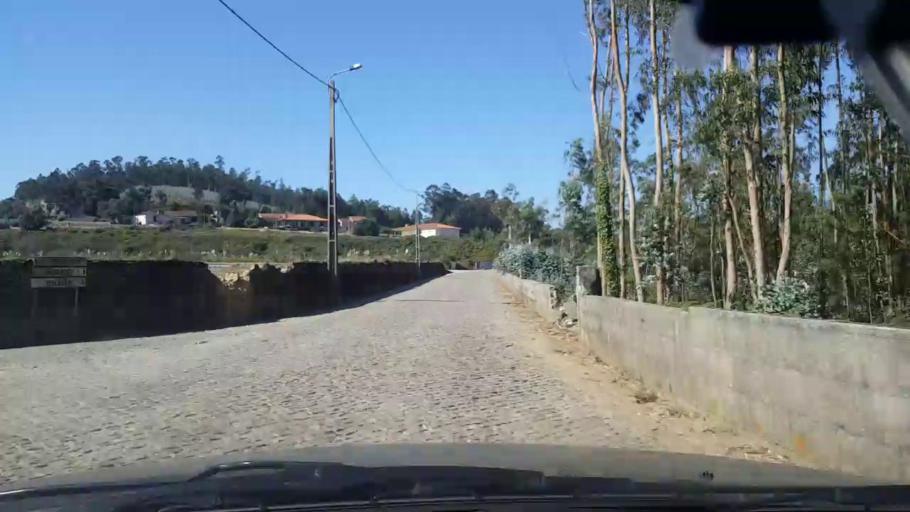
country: PT
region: Braga
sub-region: Vila Nova de Famalicao
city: Ribeirao
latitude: 41.3805
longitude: -8.6396
